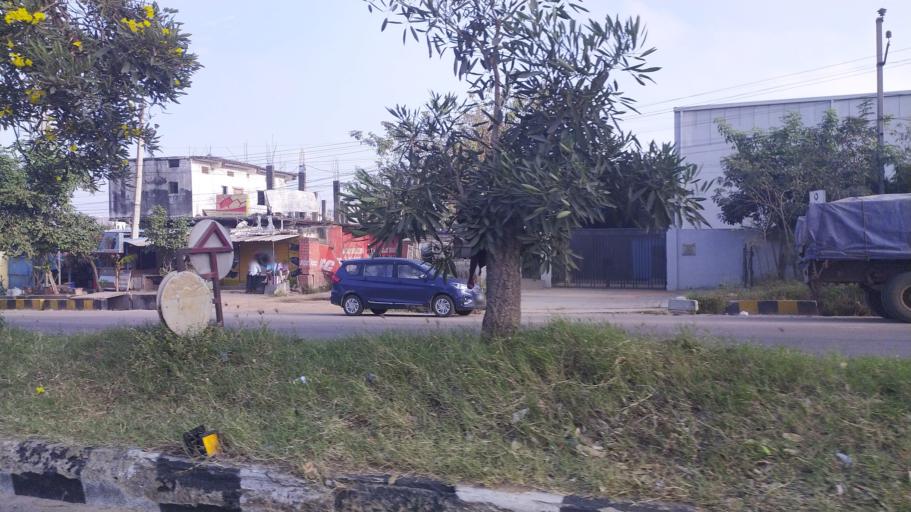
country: IN
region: Telangana
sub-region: Rangareddi
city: Balapur
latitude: 17.3178
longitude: 78.4378
